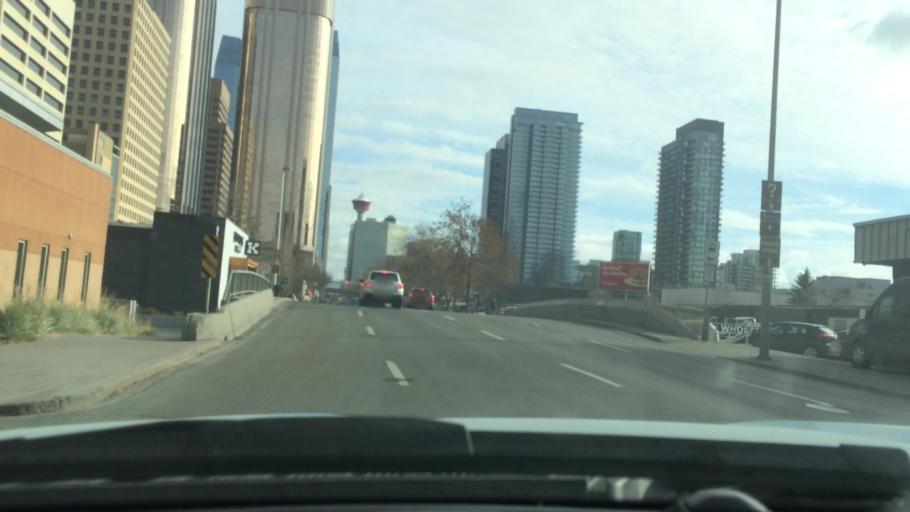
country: CA
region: Alberta
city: Calgary
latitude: 51.0452
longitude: -114.0820
